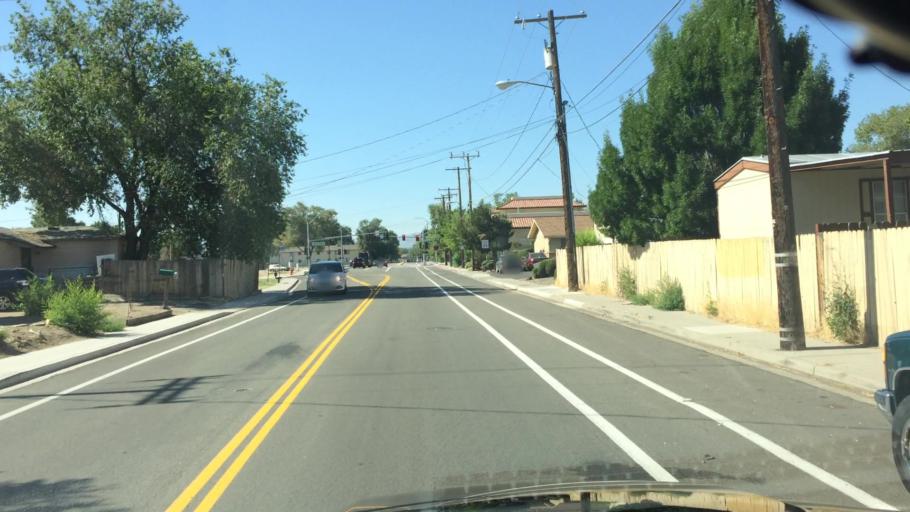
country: US
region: Nevada
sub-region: Washoe County
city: Reno
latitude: 39.4945
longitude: -119.7806
